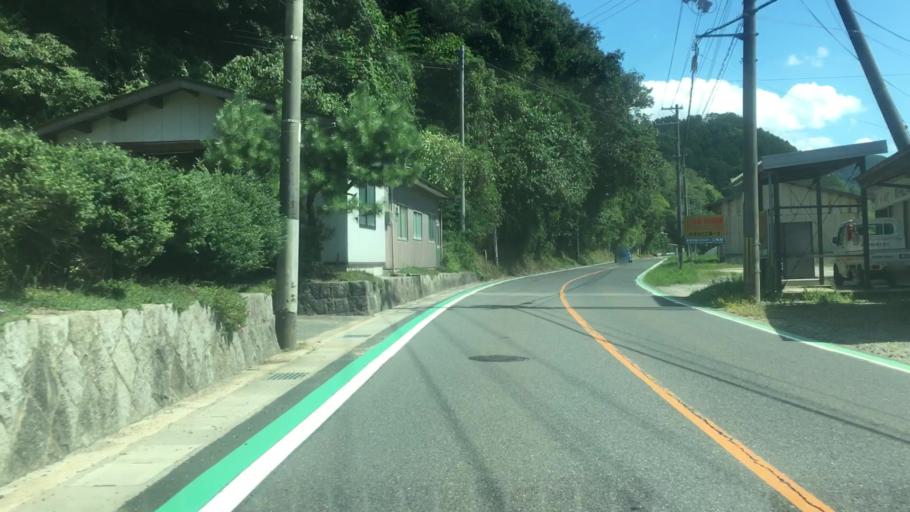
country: JP
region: Hyogo
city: Toyooka
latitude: 35.5995
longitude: 134.9035
